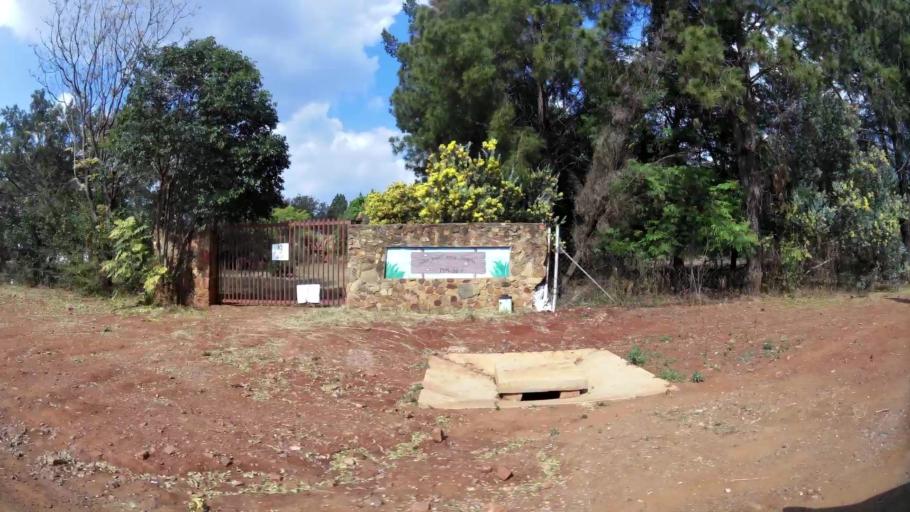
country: ZA
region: Gauteng
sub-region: City of Tshwane Metropolitan Municipality
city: Centurion
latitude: -25.8083
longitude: 28.3504
